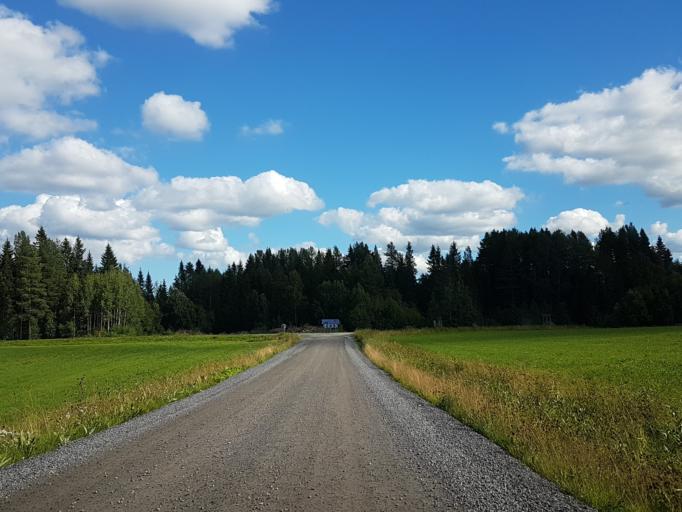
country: SE
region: Vaesterbotten
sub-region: Skelleftea Kommun
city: Burtraesk
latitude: 64.2934
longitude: 20.5215
